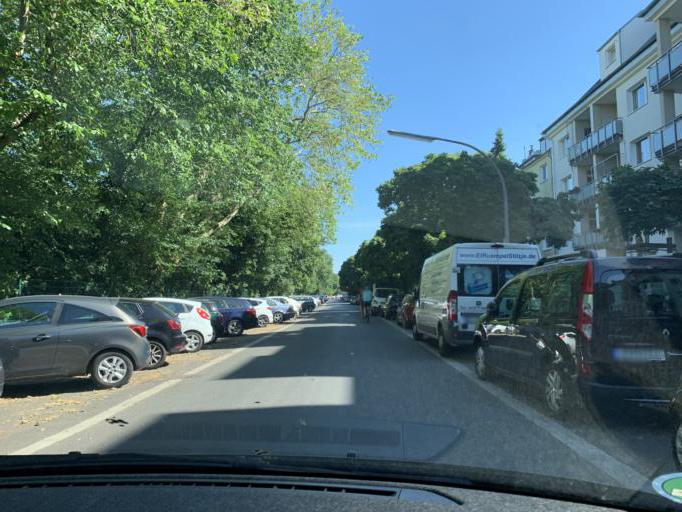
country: DE
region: North Rhine-Westphalia
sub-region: Regierungsbezirk Koln
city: Nippes
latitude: 50.9816
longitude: 6.9509
